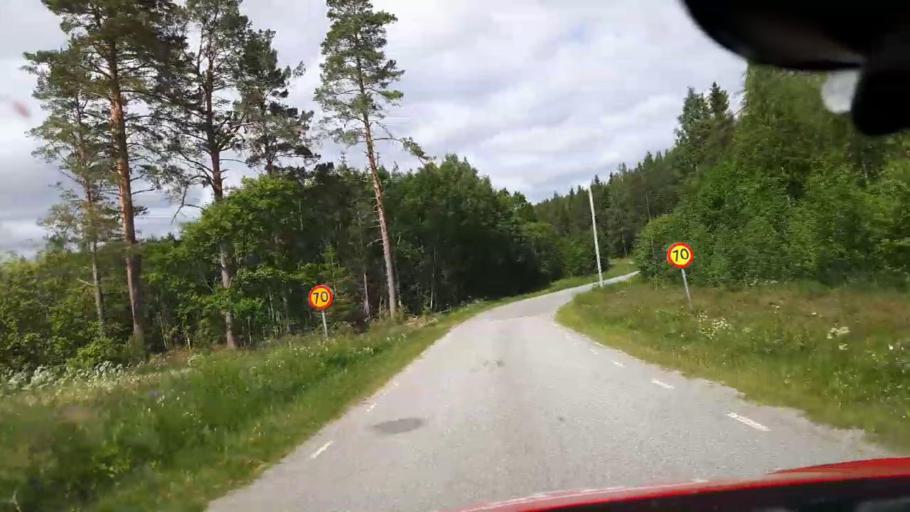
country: SE
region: Jaemtland
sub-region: Braecke Kommun
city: Braecke
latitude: 62.8544
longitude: 15.2892
